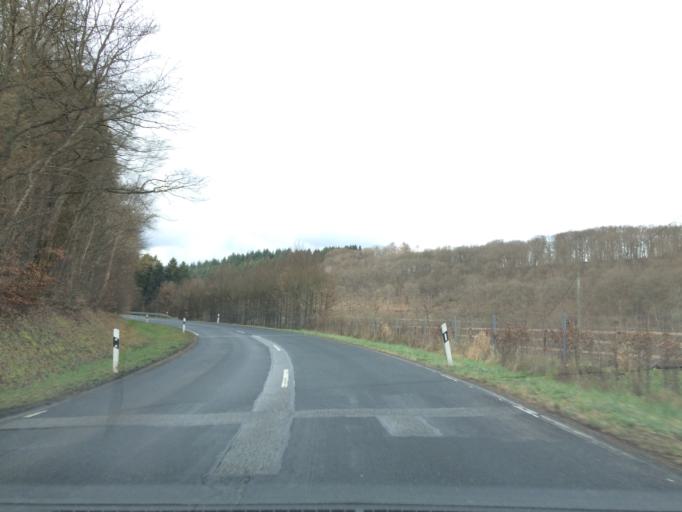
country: DE
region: Hesse
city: Weilmunster
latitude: 50.3682
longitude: 8.3933
